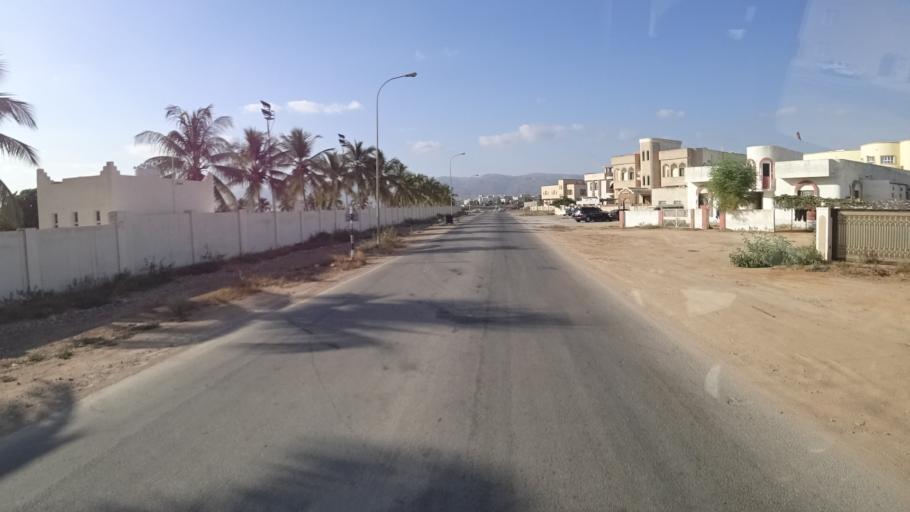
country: OM
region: Zufar
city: Salalah
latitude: 16.9943
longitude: 54.0268
